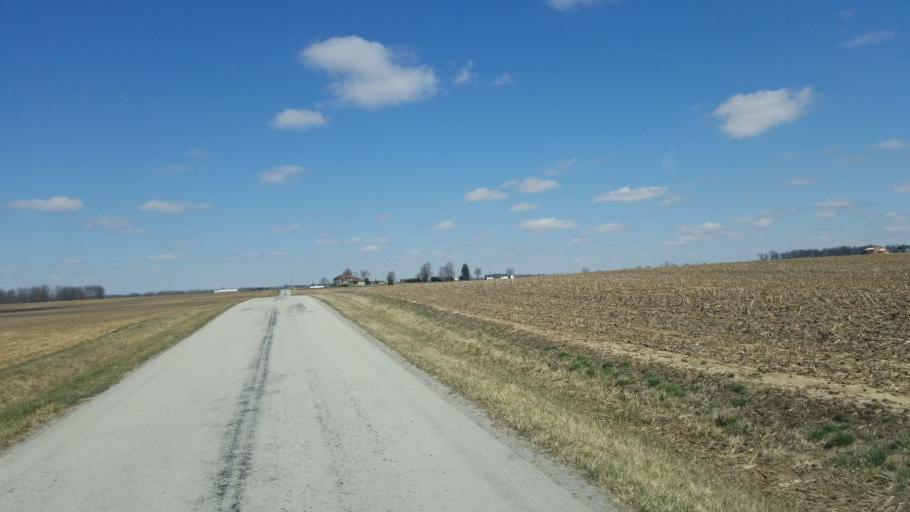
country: US
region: Ohio
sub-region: Wyandot County
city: Upper Sandusky
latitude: 40.7351
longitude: -83.1883
